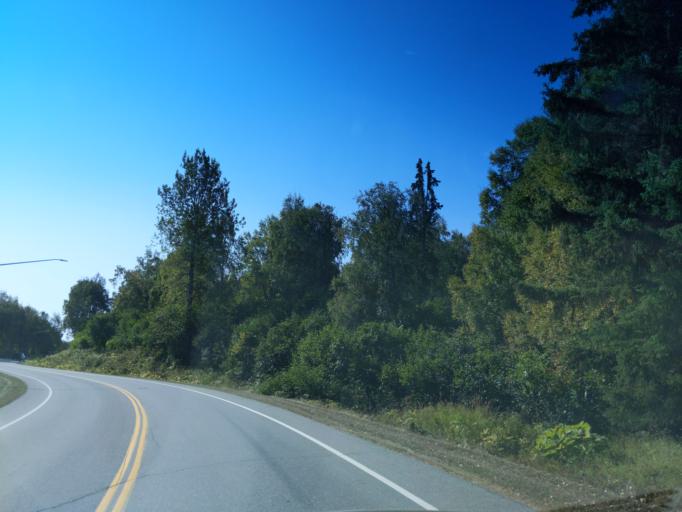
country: US
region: Alaska
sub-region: Anchorage Municipality
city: Anchorage
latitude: 61.1580
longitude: -150.0157
